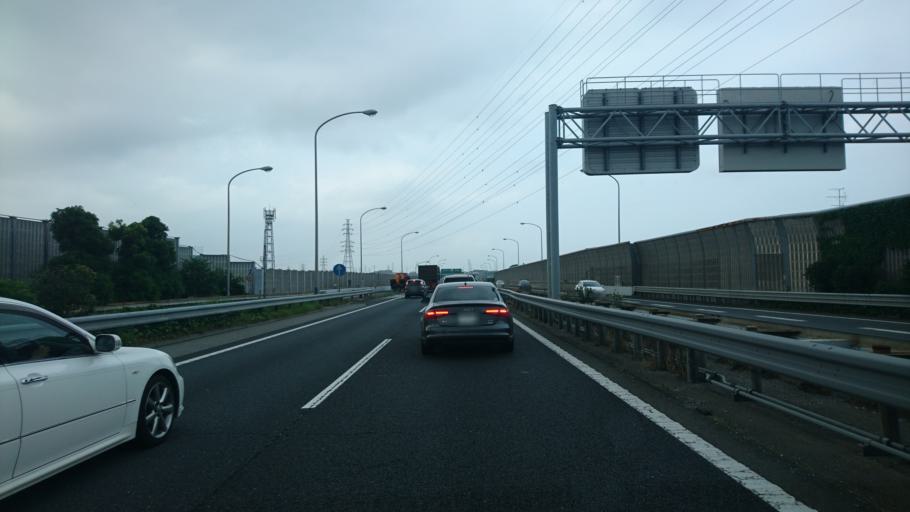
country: JP
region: Chiba
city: Chiba
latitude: 35.5976
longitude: 140.1487
